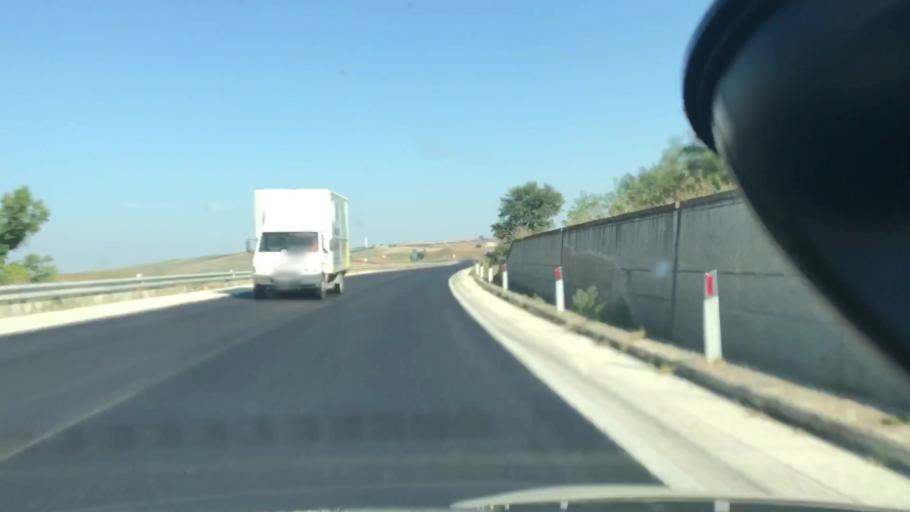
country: IT
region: Apulia
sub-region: Provincia di Barletta - Andria - Trani
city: Spinazzola
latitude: 40.9094
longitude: 16.1071
